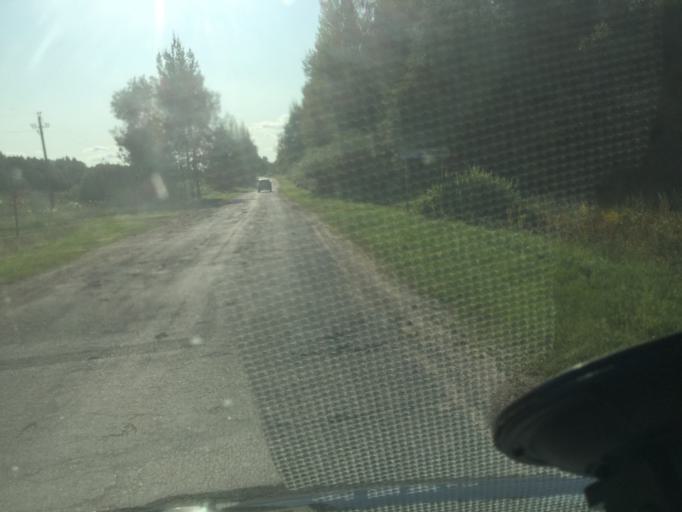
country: BY
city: Osveya
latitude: 56.0215
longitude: 28.2736
